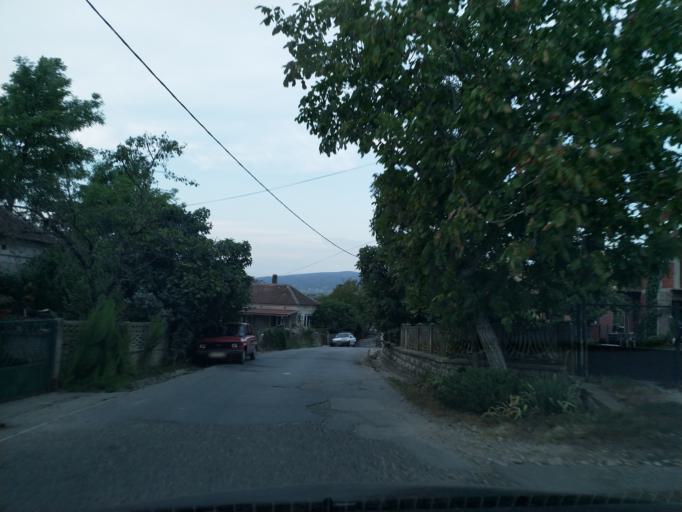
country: RS
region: Central Serbia
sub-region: Pomoravski Okrug
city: Paracin
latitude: 43.8506
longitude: 21.5280
